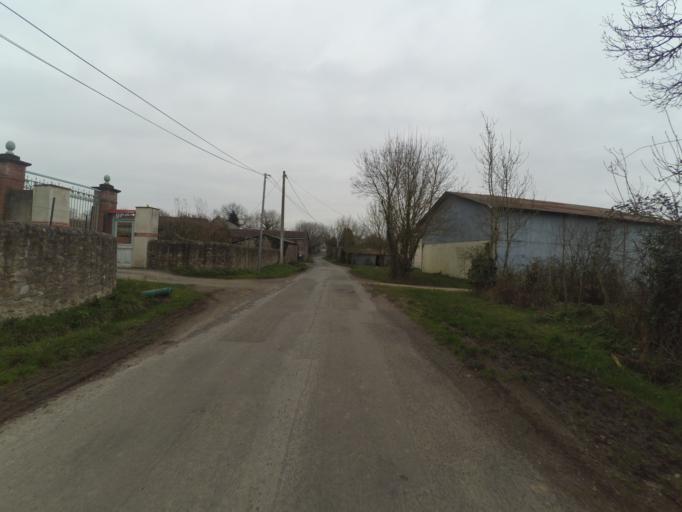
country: FR
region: Pays de la Loire
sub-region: Departement de la Loire-Atlantique
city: Coueron
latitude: 47.2383
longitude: -1.7053
